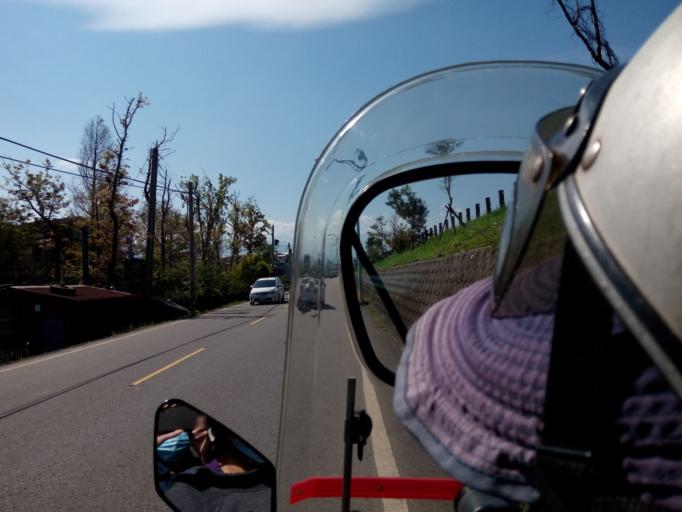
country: TW
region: Taiwan
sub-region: Yilan
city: Yilan
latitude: 24.6755
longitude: 121.7435
